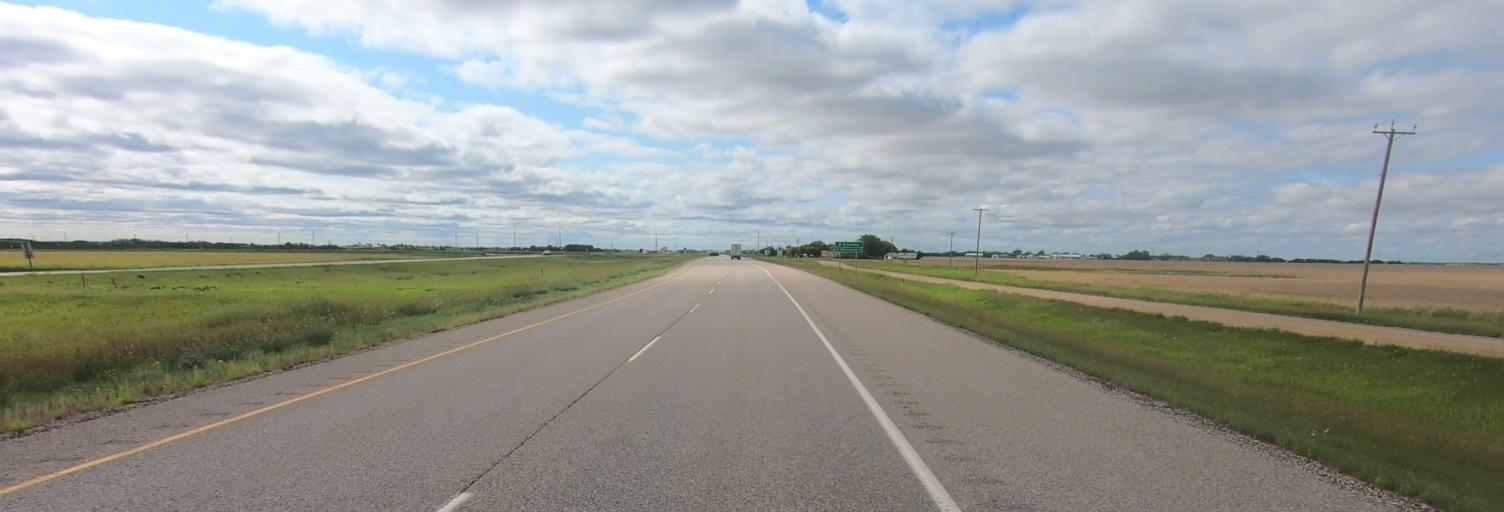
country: CA
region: Manitoba
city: Brandon
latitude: 49.8870
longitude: -99.8666
